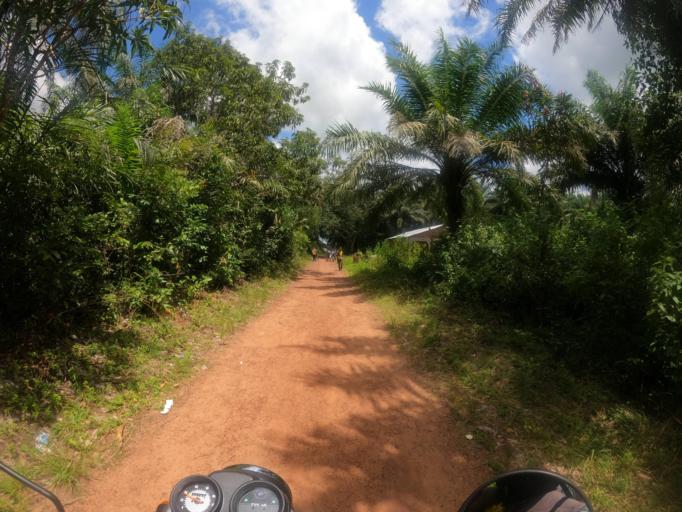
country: SL
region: Northern Province
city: Makeni
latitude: 8.8638
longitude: -12.0992
